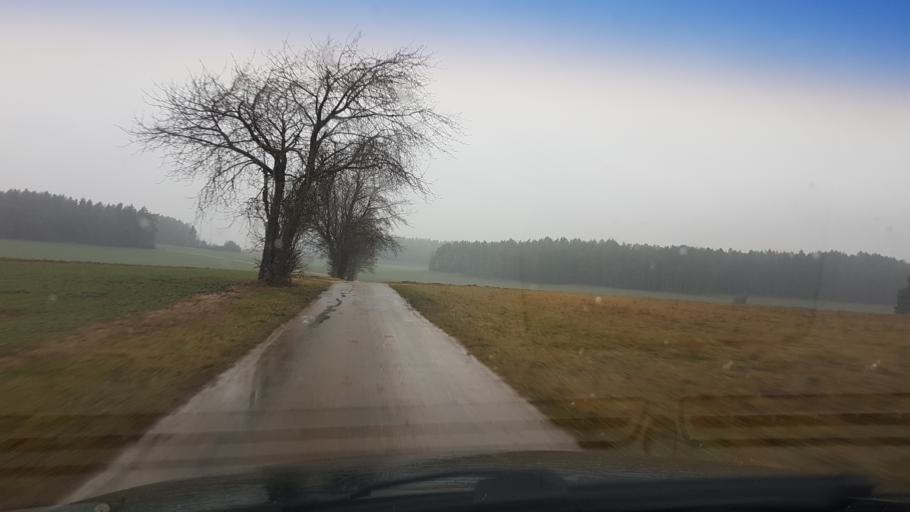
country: DE
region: Bavaria
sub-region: Upper Franconia
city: Kasendorf
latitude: 50.0340
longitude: 11.3054
